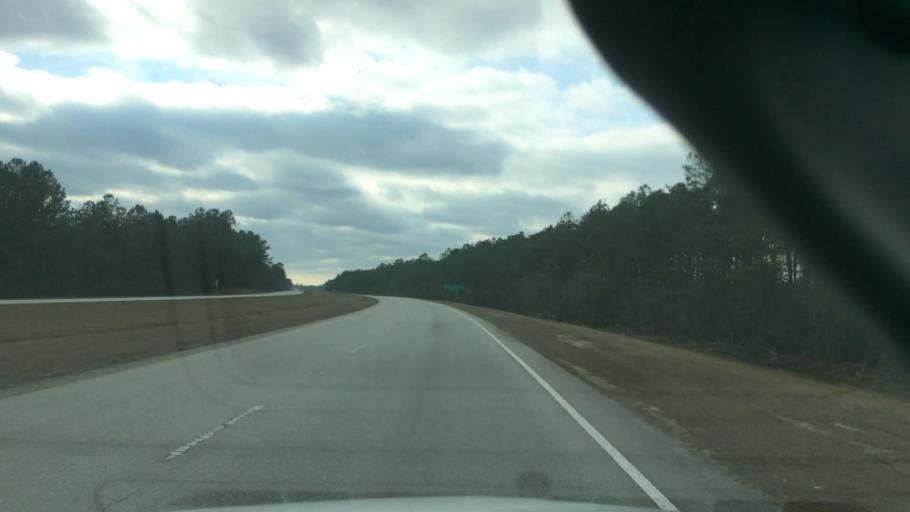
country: US
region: North Carolina
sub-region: Brunswick County
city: Bolivia
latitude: 34.0623
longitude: -78.2010
